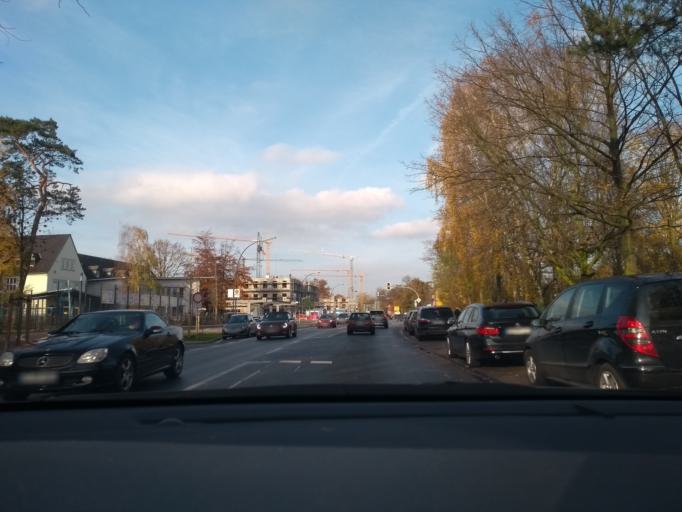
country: DE
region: North Rhine-Westphalia
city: Selm
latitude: 51.6935
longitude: 7.4668
